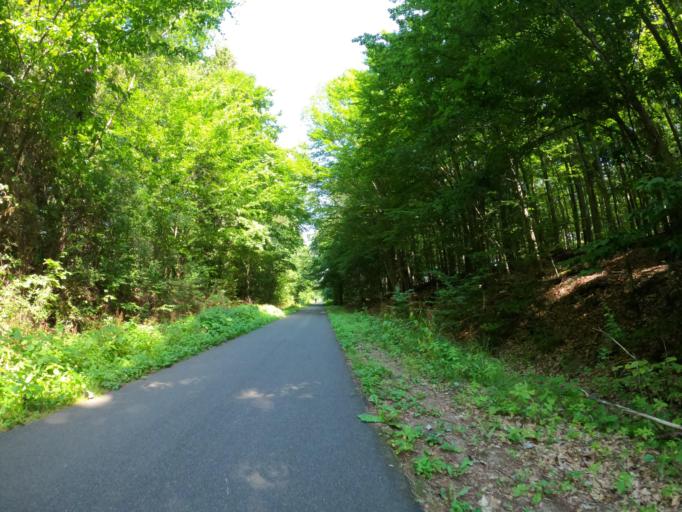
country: DE
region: Brandenburg
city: Templin
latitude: 53.2407
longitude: 13.5041
